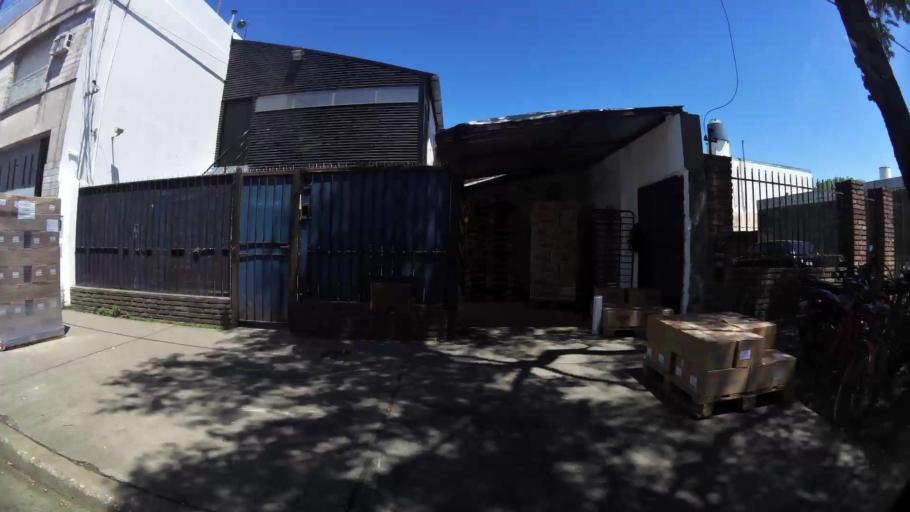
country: AR
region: Santa Fe
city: Perez
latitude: -32.9442
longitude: -60.7172
